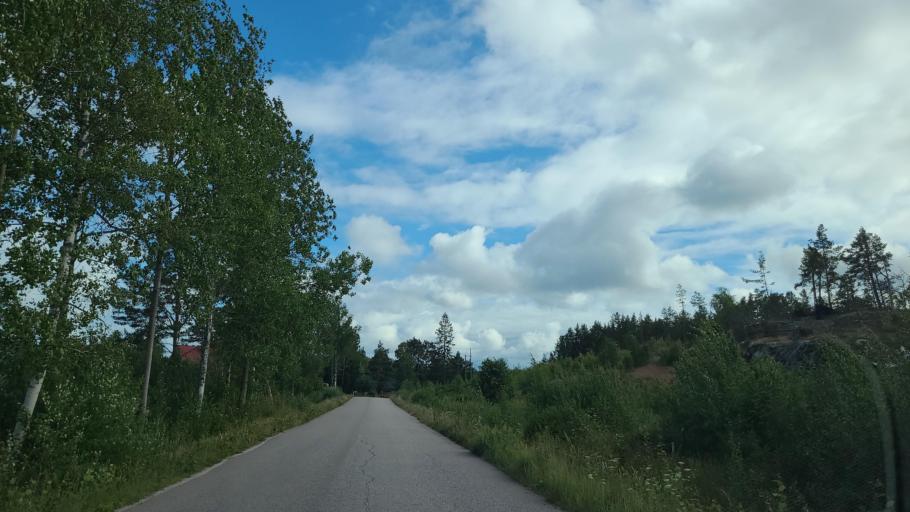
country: FI
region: Varsinais-Suomi
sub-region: Aboland-Turunmaa
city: Nagu
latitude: 60.1587
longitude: 21.7550
